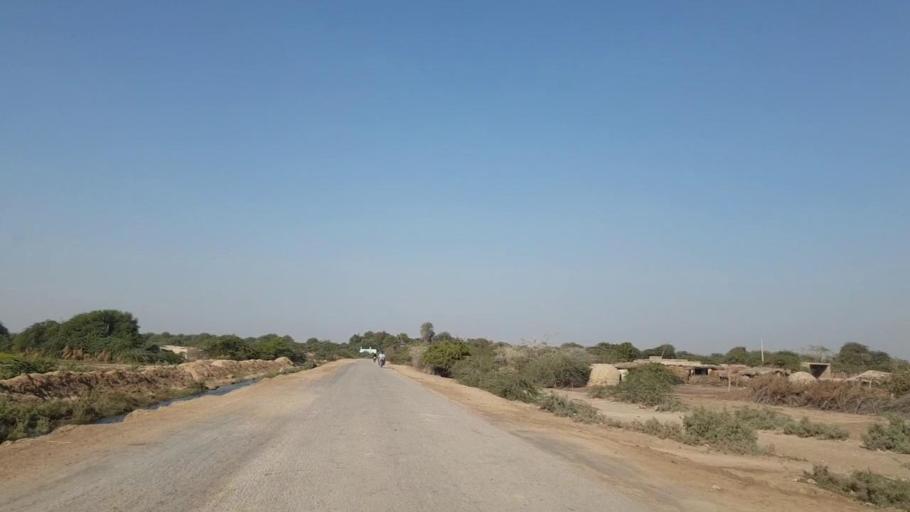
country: PK
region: Sindh
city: Digri
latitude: 25.1203
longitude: 69.1082
